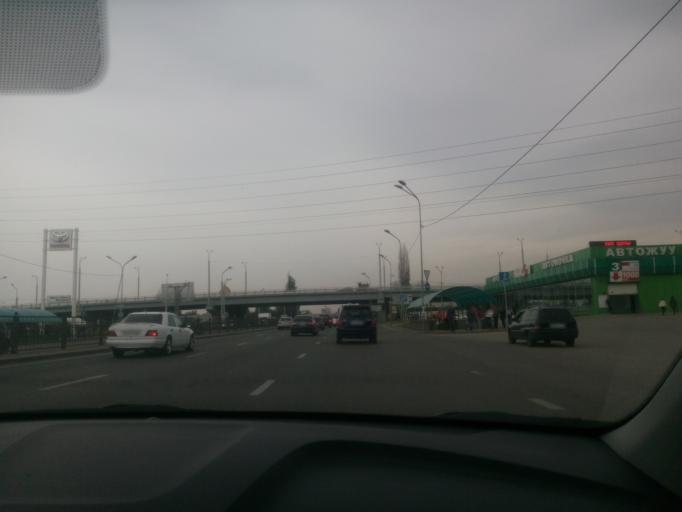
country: KZ
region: Almaty Qalasy
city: Almaty
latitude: 43.2434
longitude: 76.8265
